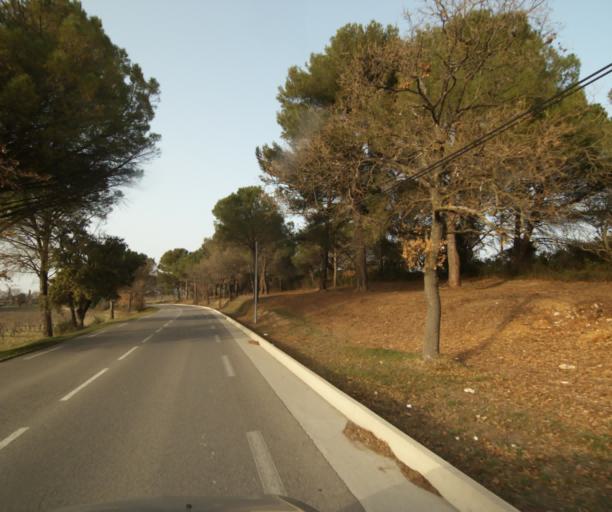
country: FR
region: Provence-Alpes-Cote d'Azur
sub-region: Departement des Bouches-du-Rhone
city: Eguilles
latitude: 43.5907
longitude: 5.3674
